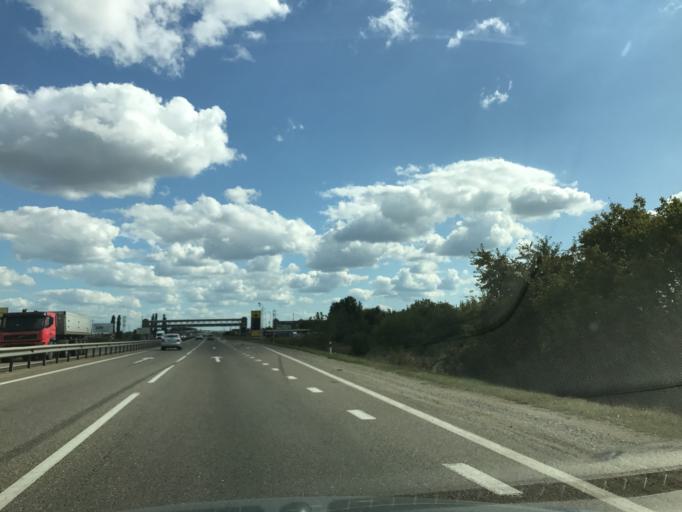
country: RU
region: Adygeya
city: Adygeysk
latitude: 44.9159
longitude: 39.1490
